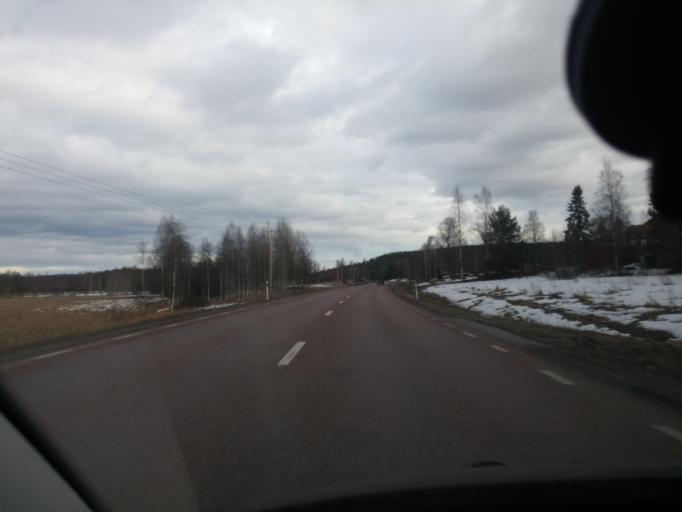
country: SE
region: Gaevleborg
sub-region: Ljusdals Kommun
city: Ljusdal
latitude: 61.8133
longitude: 16.0874
